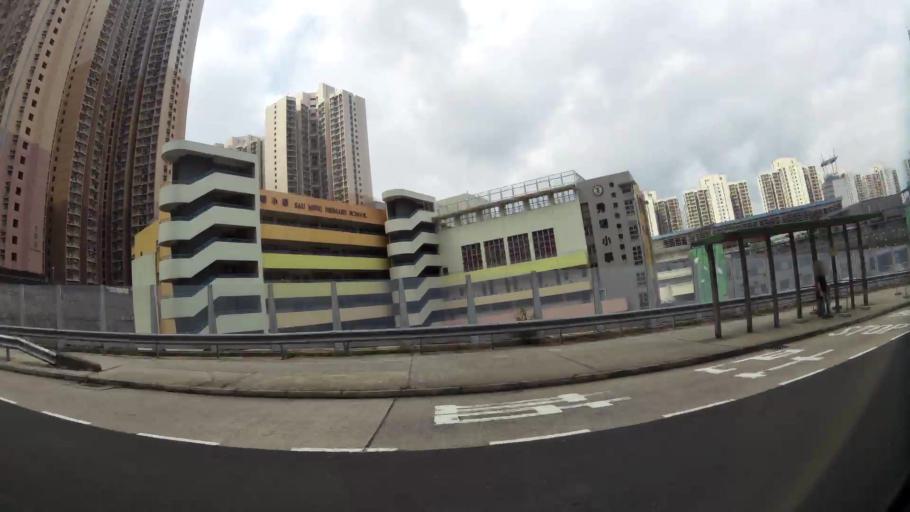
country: HK
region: Kowloon City
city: Kowloon
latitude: 22.3199
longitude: 114.2334
